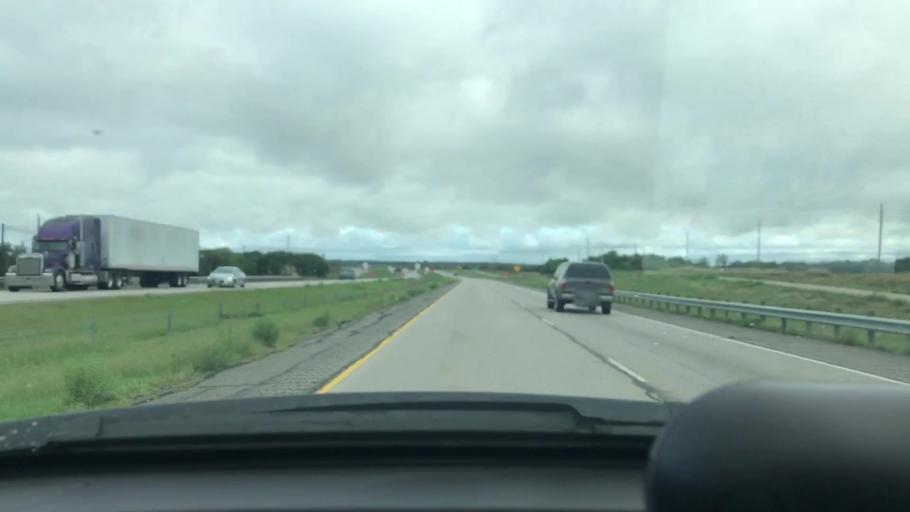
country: US
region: Texas
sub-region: Collin County
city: Anna
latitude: 33.3729
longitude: -96.5814
